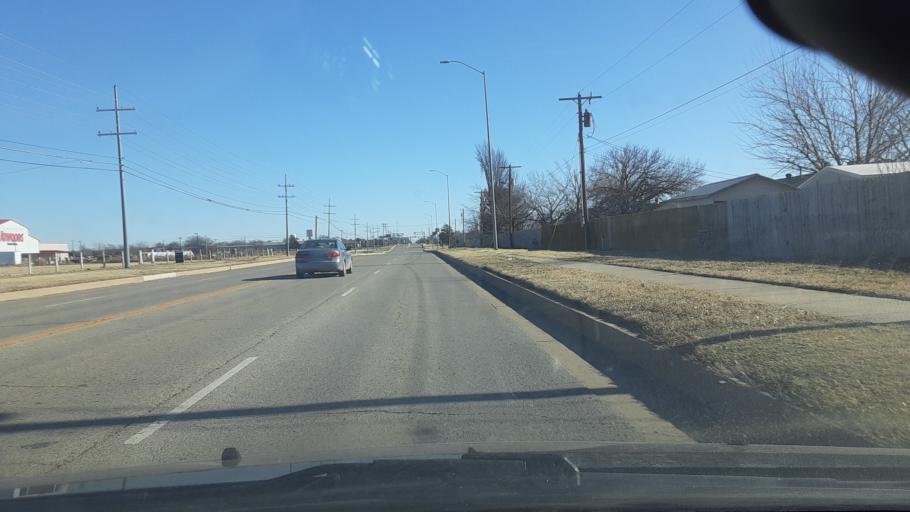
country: US
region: Oklahoma
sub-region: Kay County
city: Ponca City
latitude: 36.7386
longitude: -97.0815
